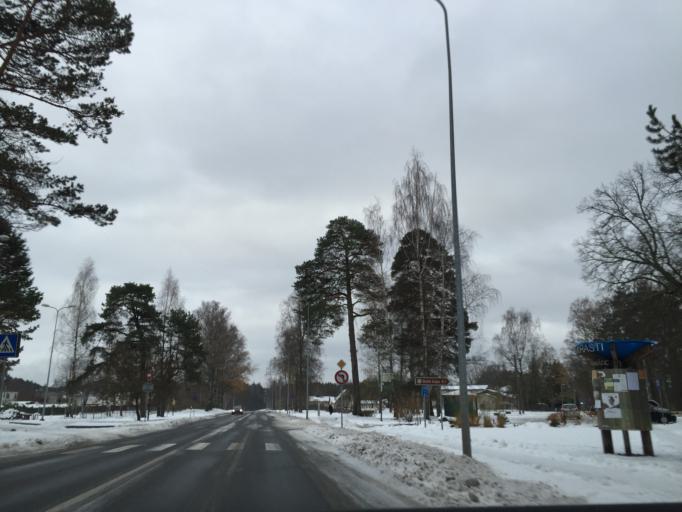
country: LV
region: Saulkrastu
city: Saulkrasti
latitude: 57.2341
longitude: 24.3941
